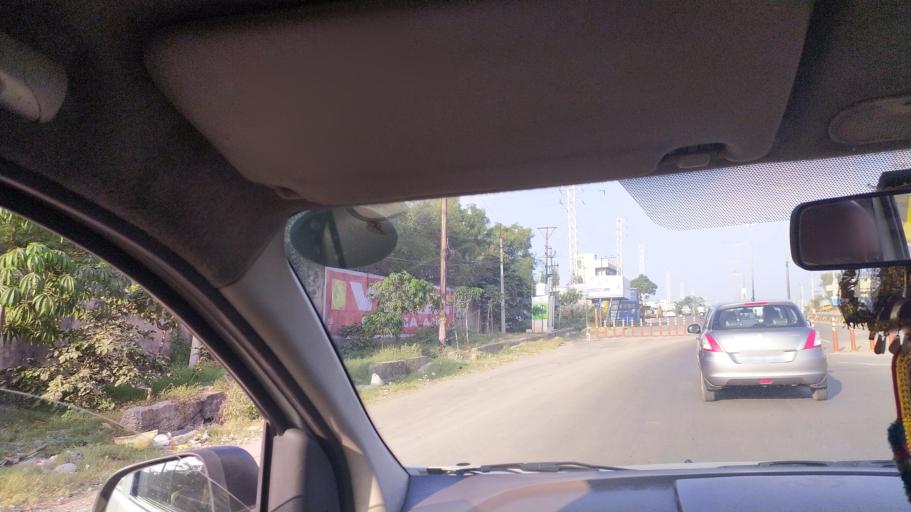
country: IN
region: Telangana
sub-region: Rangareddi
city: Balapur
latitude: 17.3154
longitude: 78.4569
